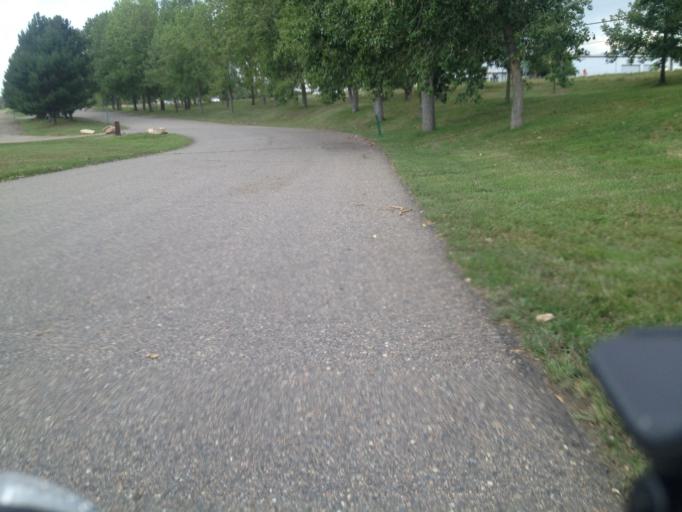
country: US
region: Colorado
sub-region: Boulder County
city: Louisville
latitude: 39.9834
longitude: -105.1272
